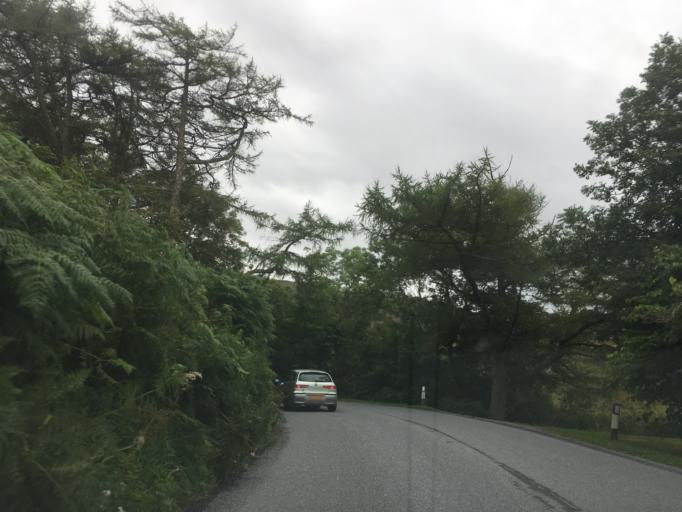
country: GB
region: Scotland
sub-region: Argyll and Bute
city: Oban
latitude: 56.2658
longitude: -5.4793
